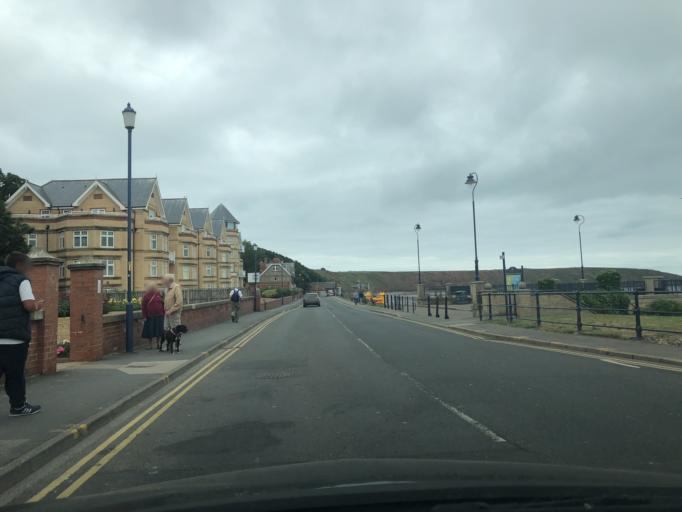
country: GB
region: England
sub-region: North Yorkshire
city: Filey
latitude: 54.2089
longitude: -0.2849
